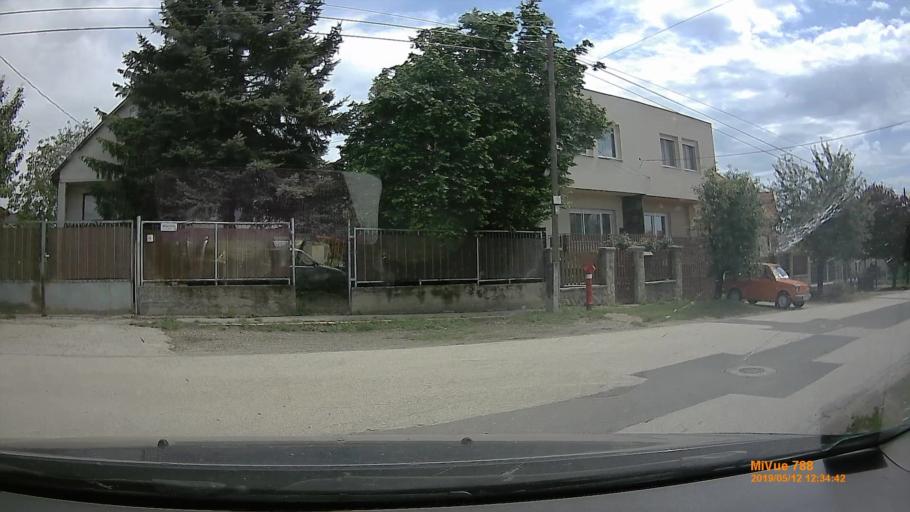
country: HU
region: Pest
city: Ecser
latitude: 47.4590
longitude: 19.3142
